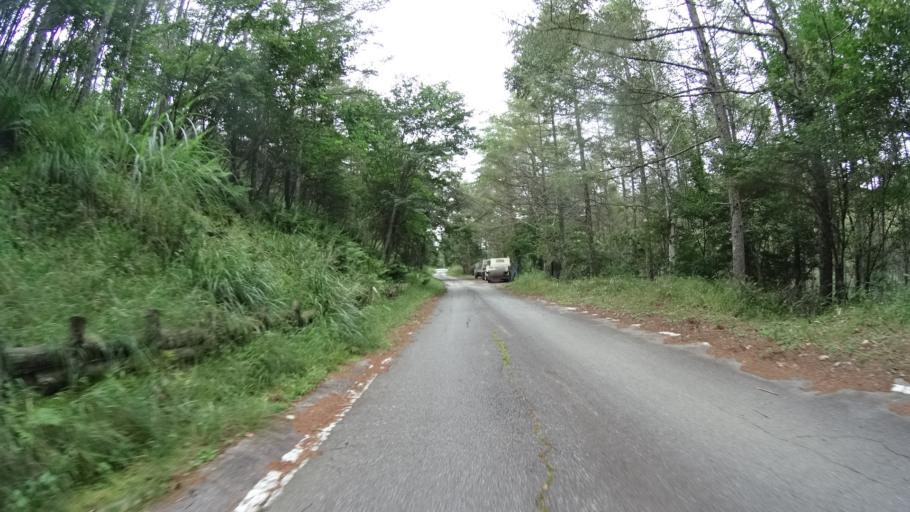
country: JP
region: Yamanashi
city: Kofu-shi
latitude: 35.8286
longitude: 138.5579
